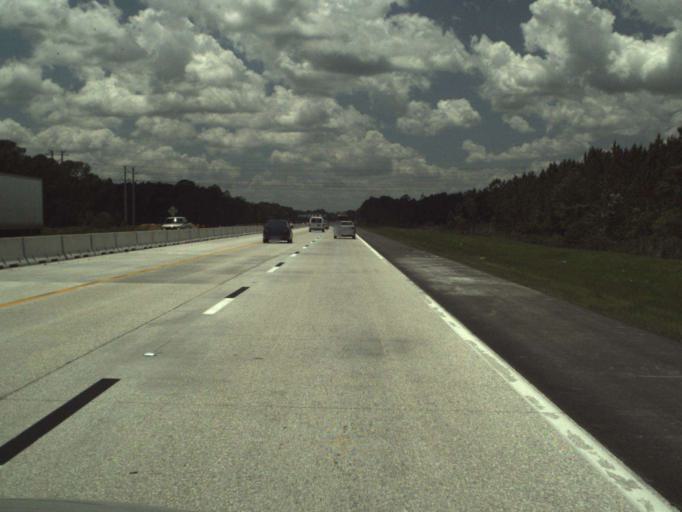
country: US
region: Florida
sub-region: Volusia County
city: South Daytona
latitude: 29.1446
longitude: -81.1016
